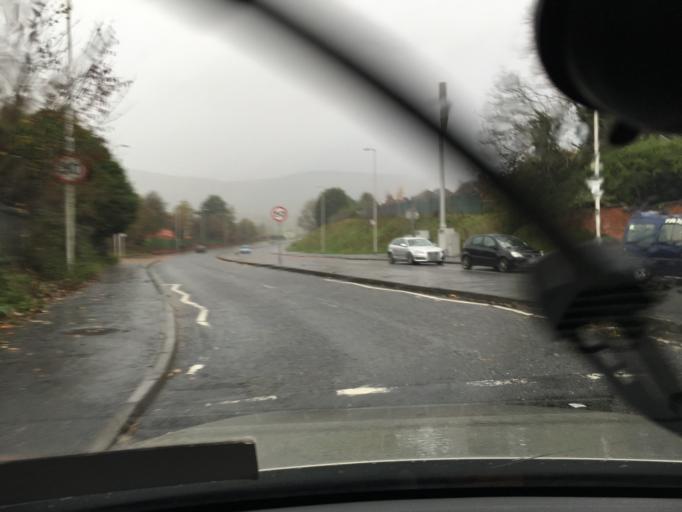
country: GB
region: Northern Ireland
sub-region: City of Belfast
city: Belfast
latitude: 54.5816
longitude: -5.9888
